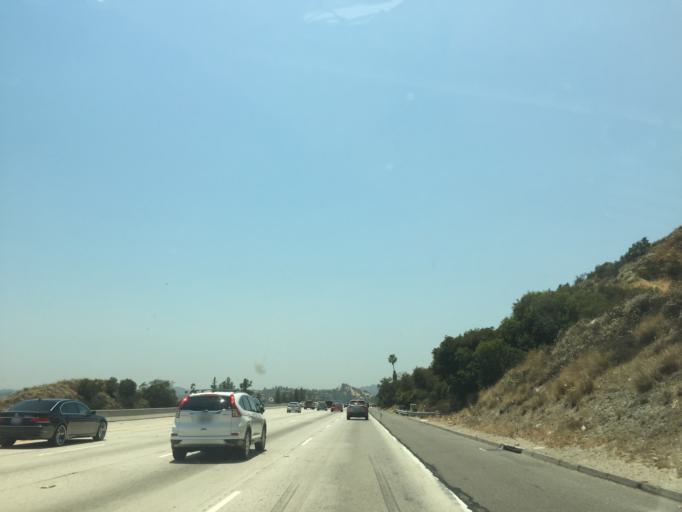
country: US
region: California
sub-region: Los Angeles County
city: Glendale
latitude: 34.1471
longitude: -118.2033
